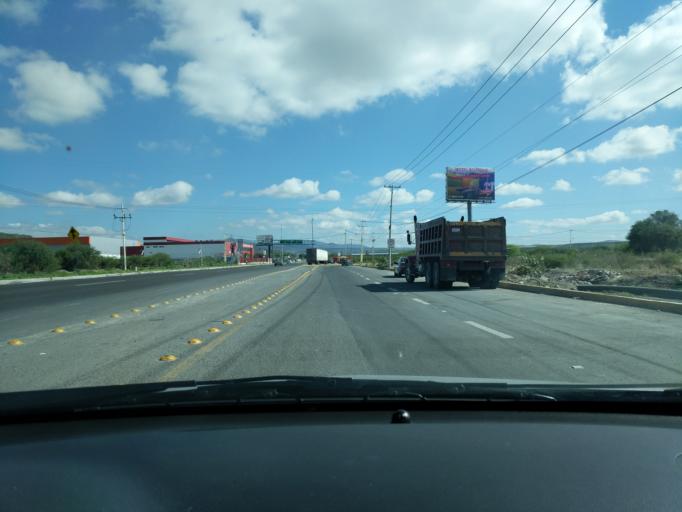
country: MX
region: Queretaro
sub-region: Queretaro
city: Patria Nueva
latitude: 20.6376
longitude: -100.4999
